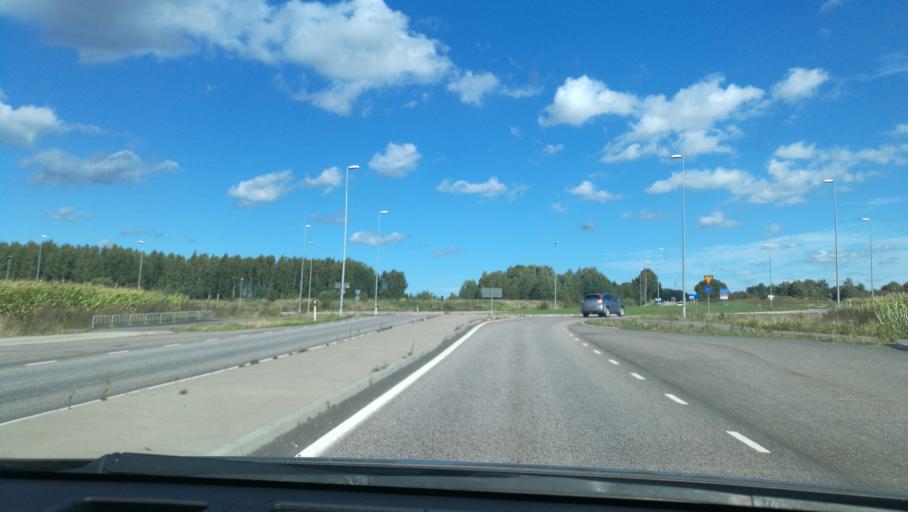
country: SE
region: Vaestra Goetaland
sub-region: Gotene Kommun
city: Kallby
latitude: 58.4998
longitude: 13.3028
